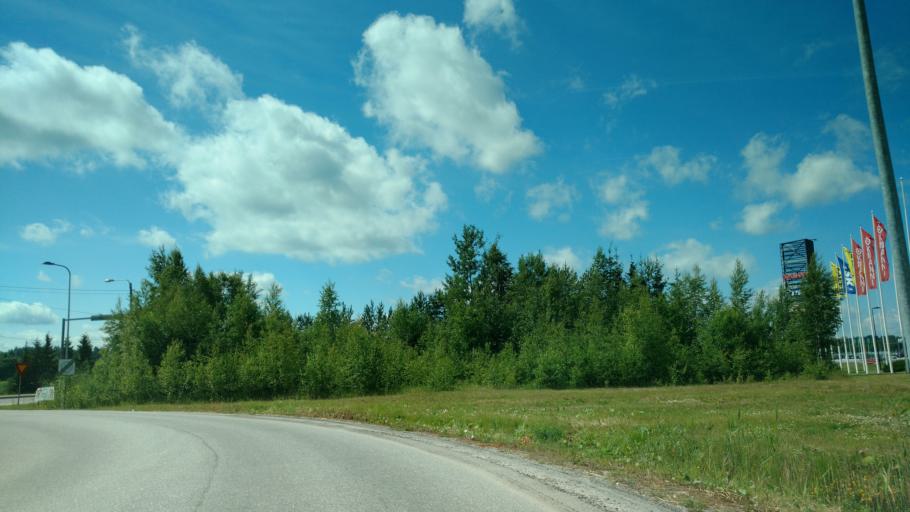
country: FI
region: Varsinais-Suomi
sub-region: Salo
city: Halikko
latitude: 60.3920
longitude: 23.0910
